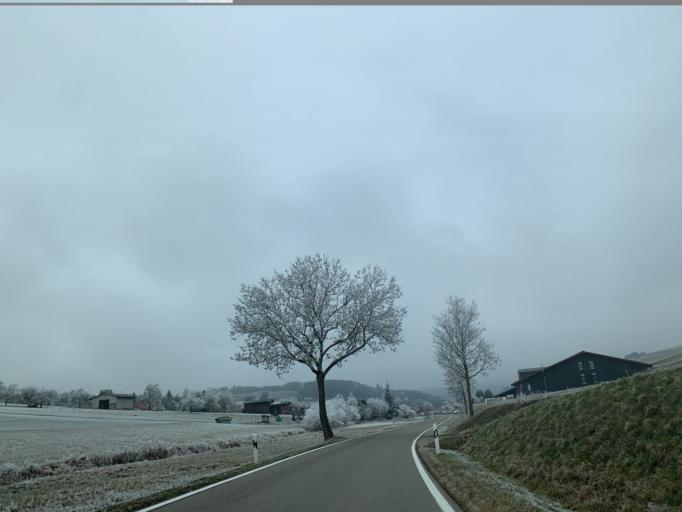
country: DE
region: Baden-Wuerttemberg
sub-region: Freiburg Region
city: Tengen
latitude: 47.8618
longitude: 8.6757
